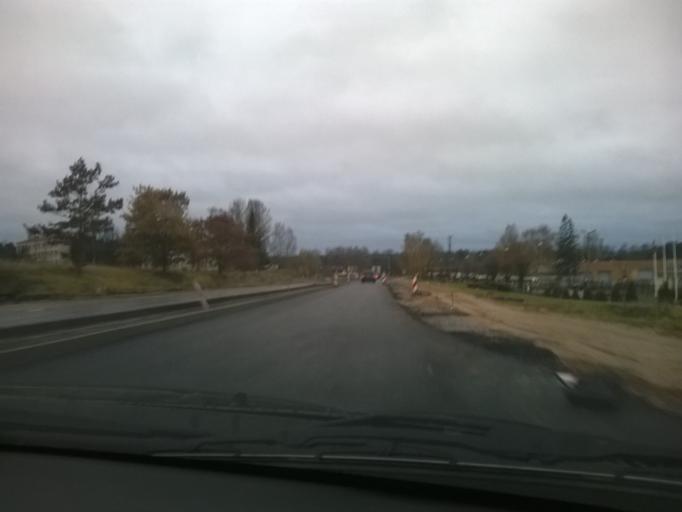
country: LV
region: Koceni
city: Koceni
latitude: 57.5212
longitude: 25.3670
